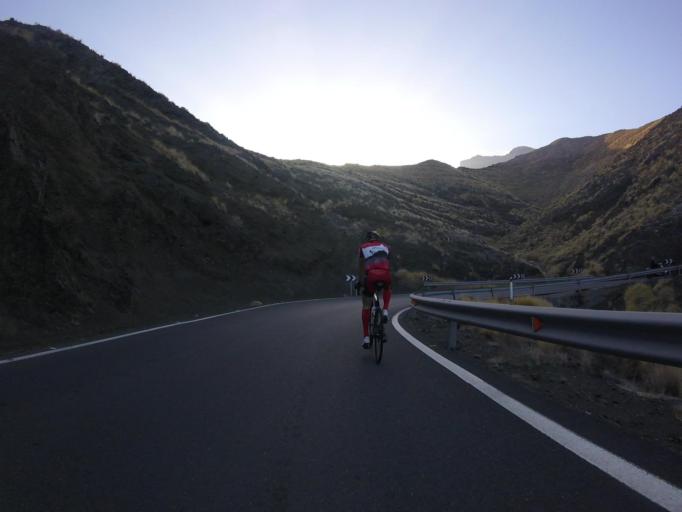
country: ES
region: Canary Islands
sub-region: Provincia de Las Palmas
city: Agaete
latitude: 28.0758
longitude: -15.7085
